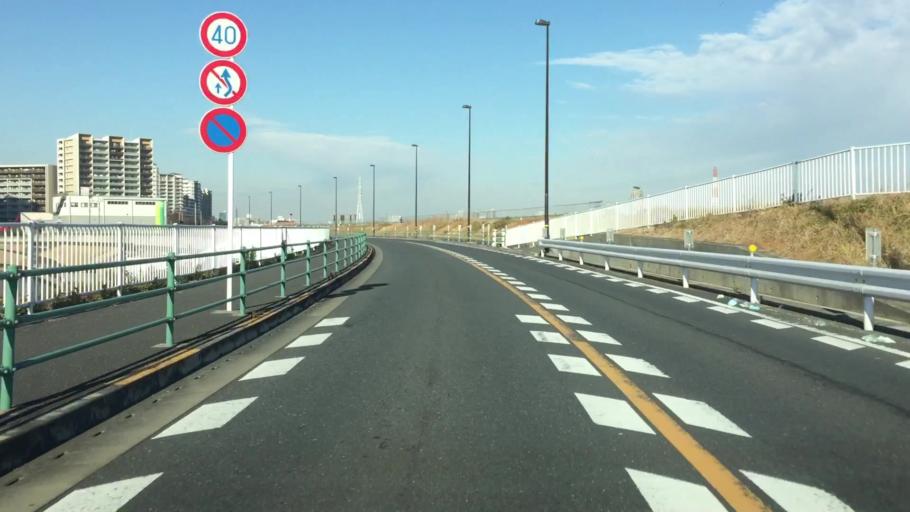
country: JP
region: Saitama
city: Kawaguchi
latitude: 35.7678
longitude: 139.7559
